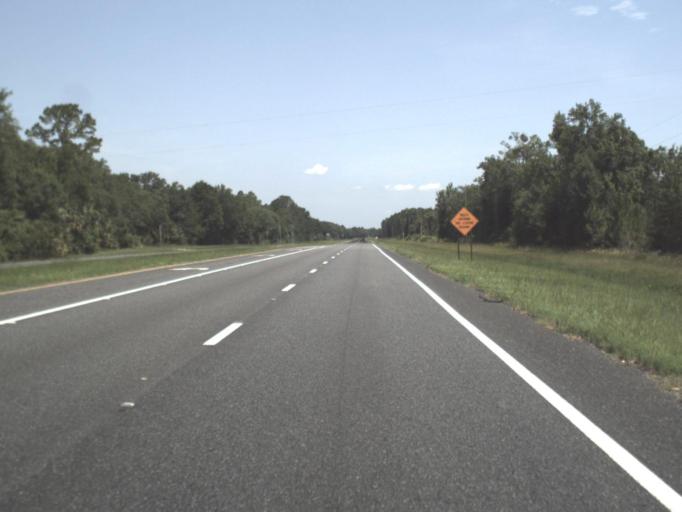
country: US
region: Florida
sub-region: Taylor County
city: Steinhatchee
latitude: 29.7369
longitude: -83.3165
